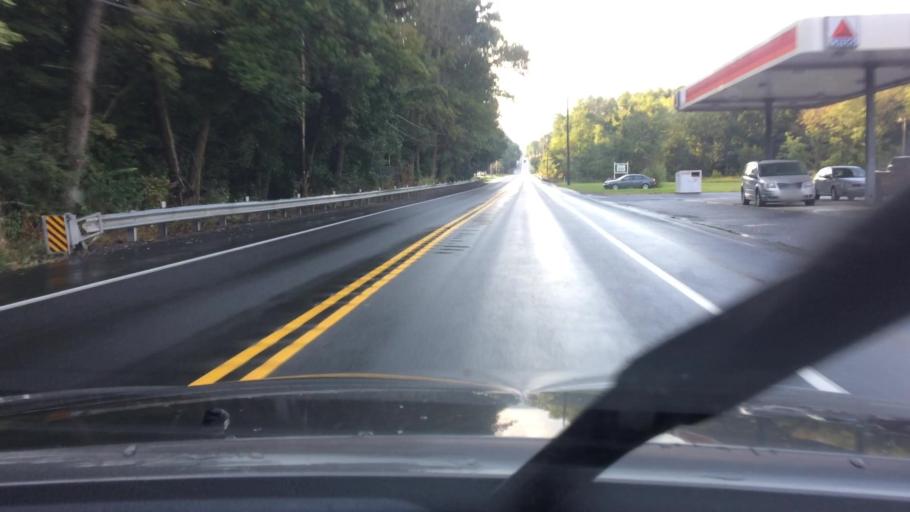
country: US
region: Pennsylvania
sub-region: Lehigh County
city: Schnecksville
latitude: 40.6868
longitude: -75.7450
